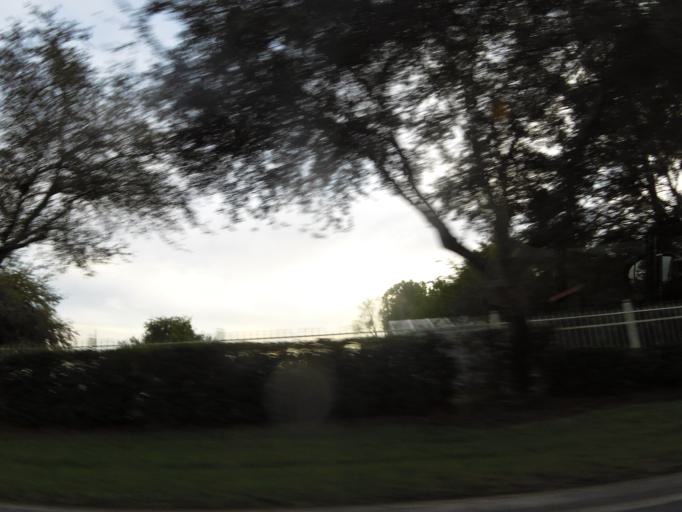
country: US
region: Florida
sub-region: Saint Johns County
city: Fruit Cove
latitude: 30.1583
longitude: -81.5383
